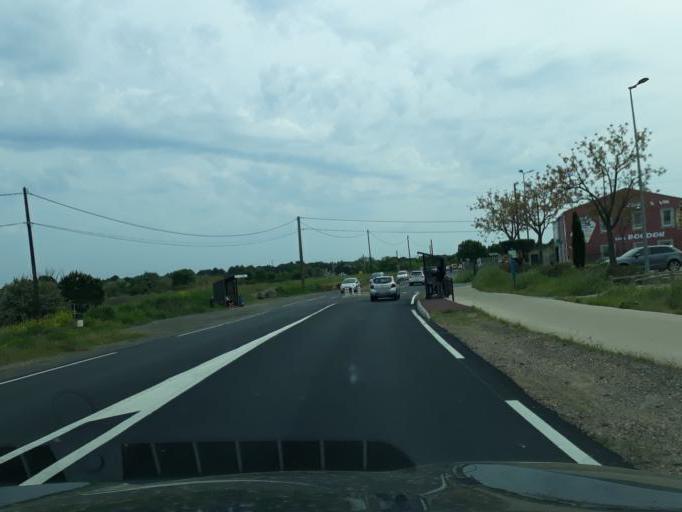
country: FR
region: Languedoc-Roussillon
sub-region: Departement de l'Herault
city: Agde
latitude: 43.2955
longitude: 3.4710
